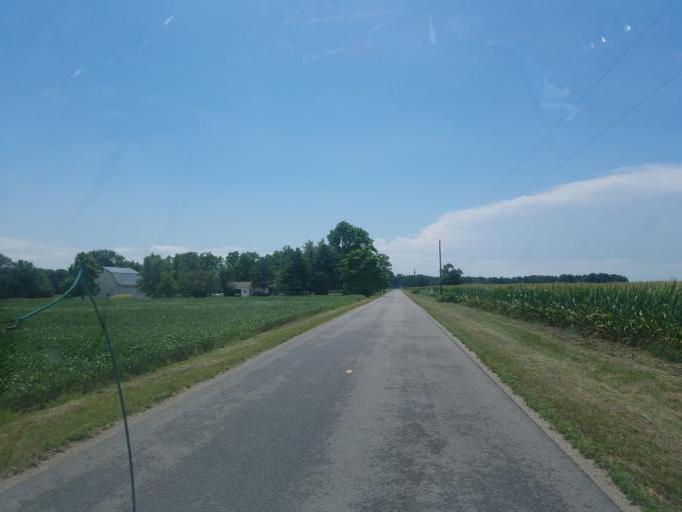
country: US
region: Ohio
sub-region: Paulding County
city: Antwerp
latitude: 41.1873
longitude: -84.7768
